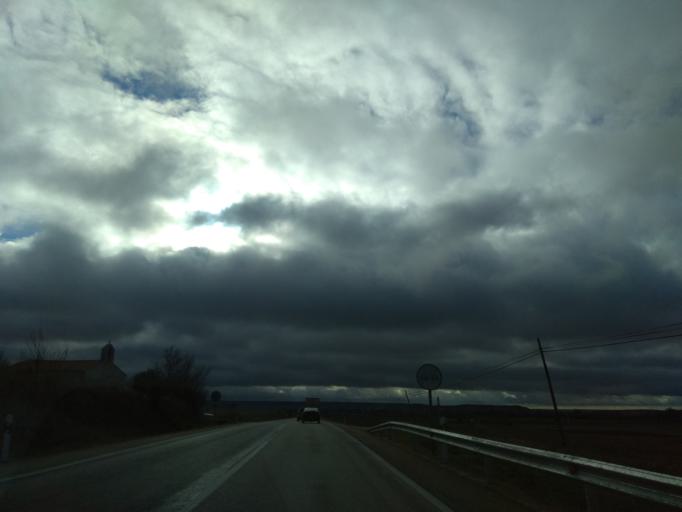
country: ES
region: Castille and Leon
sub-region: Provincia de Burgos
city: Quintanaortuno
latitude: 42.4855
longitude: -3.6954
